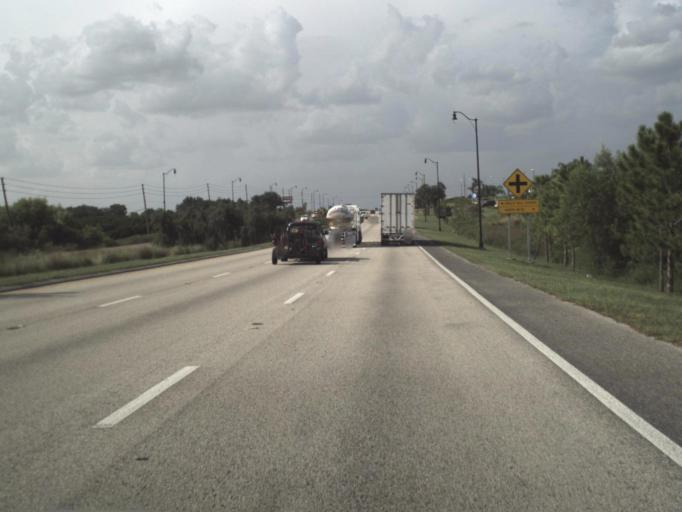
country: US
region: Florida
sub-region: Polk County
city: Davenport
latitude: 28.1612
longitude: -81.6396
